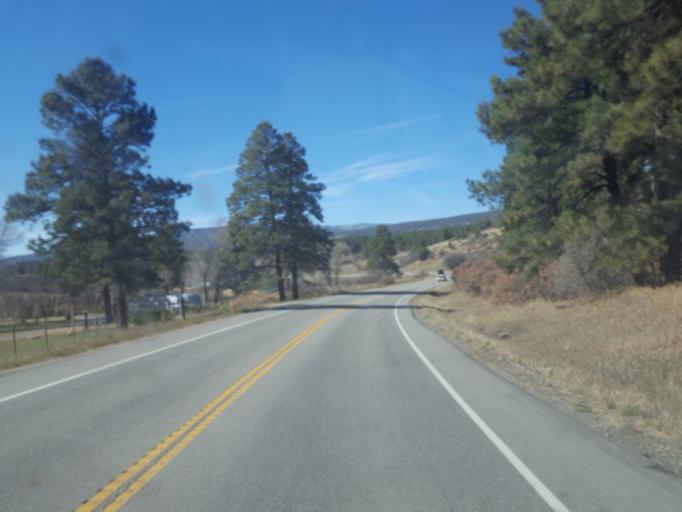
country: US
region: Colorado
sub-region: Archuleta County
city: Pagosa Springs
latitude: 37.2389
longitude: -107.1378
